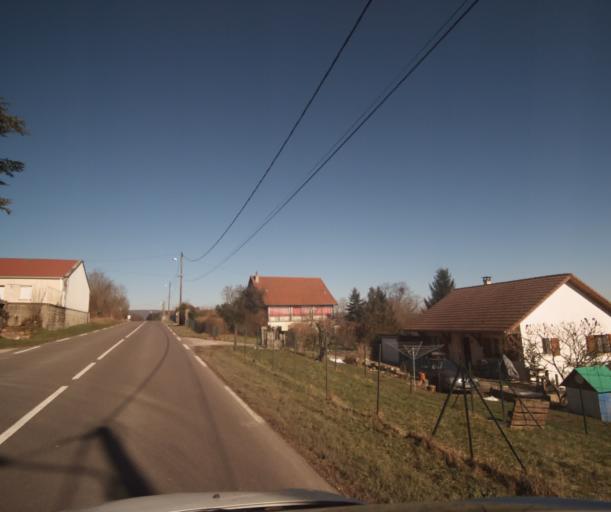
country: FR
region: Franche-Comte
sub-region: Departement du Doubs
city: Thise
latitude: 47.2713
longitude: 6.0550
